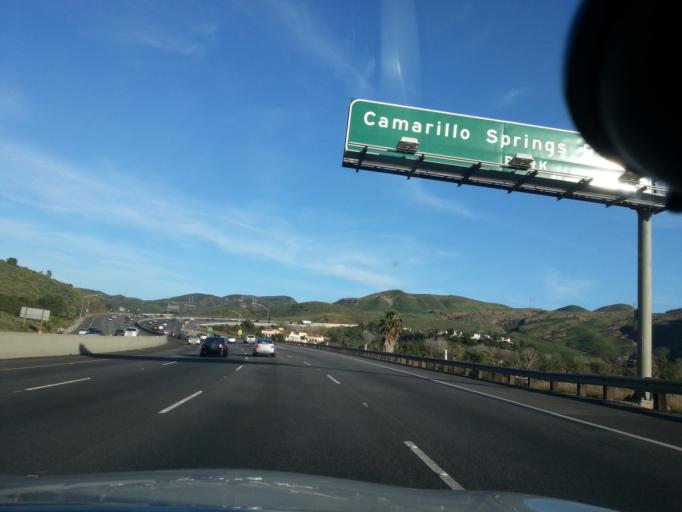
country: US
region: California
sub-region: Ventura County
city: Casa Conejo
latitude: 34.2053
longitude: -118.9886
